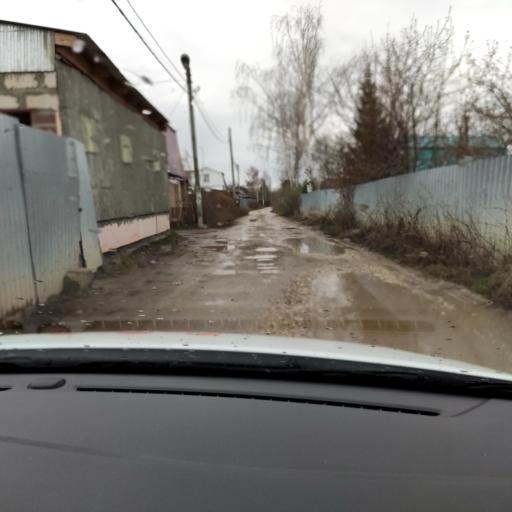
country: RU
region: Tatarstan
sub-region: Gorod Kazan'
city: Kazan
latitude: 55.6892
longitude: 49.0707
